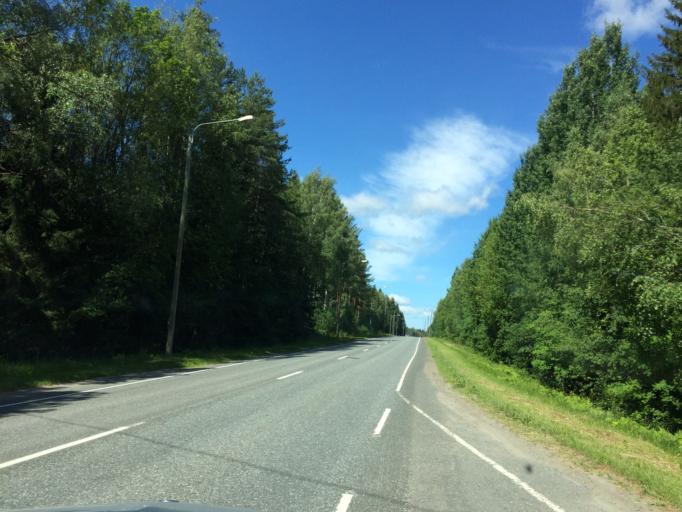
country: FI
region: Haeme
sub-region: Haemeenlinna
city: Haemeenlinna
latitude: 60.9507
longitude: 24.5049
